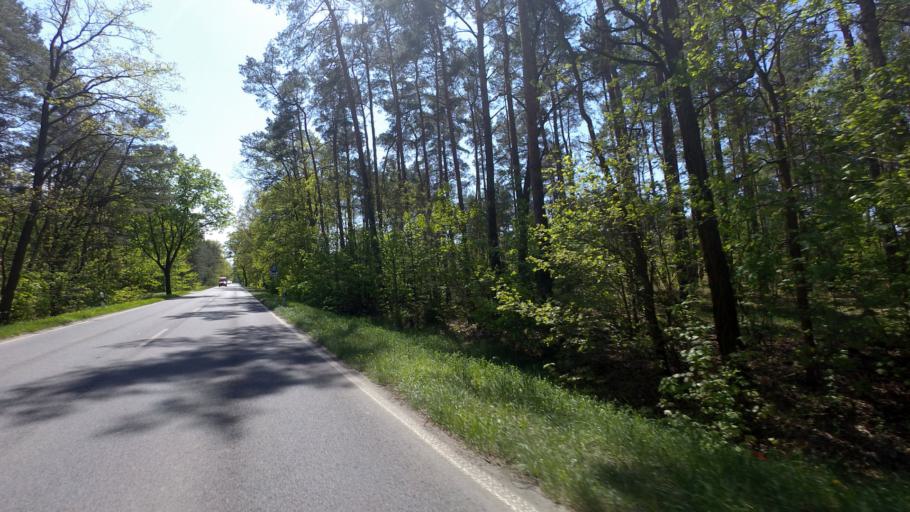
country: DE
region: Brandenburg
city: Bestensee
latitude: 52.2516
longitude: 13.6566
